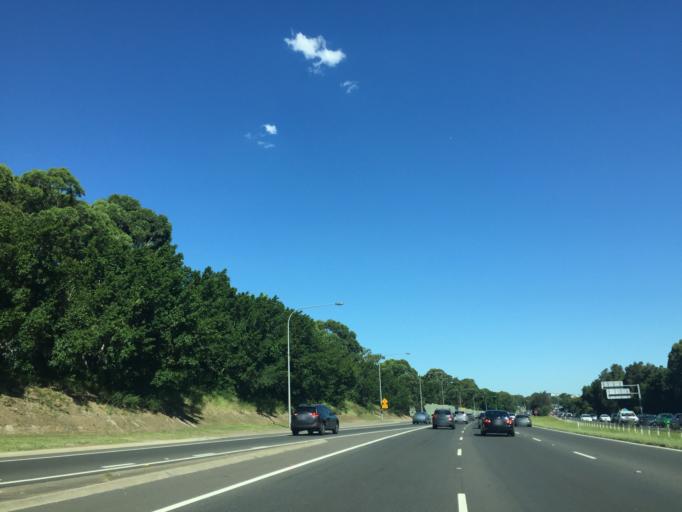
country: AU
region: New South Wales
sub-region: Auburn
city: Auburn
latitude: -33.8438
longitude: 151.0460
